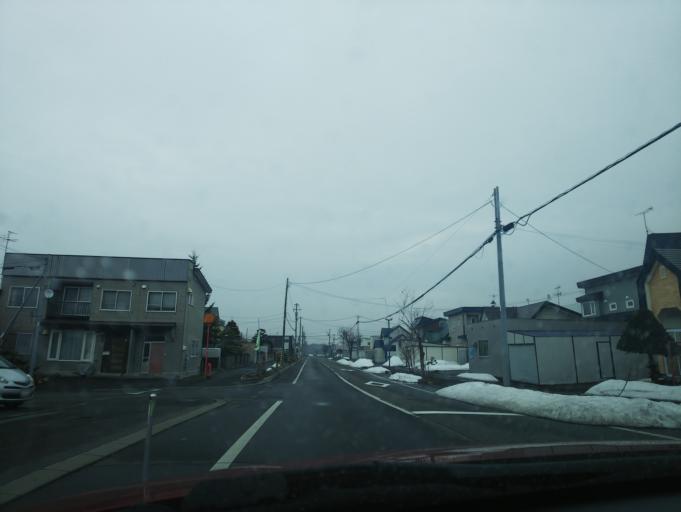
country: JP
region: Hokkaido
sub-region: Asahikawa-shi
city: Asahikawa
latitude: 43.7479
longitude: 142.3384
